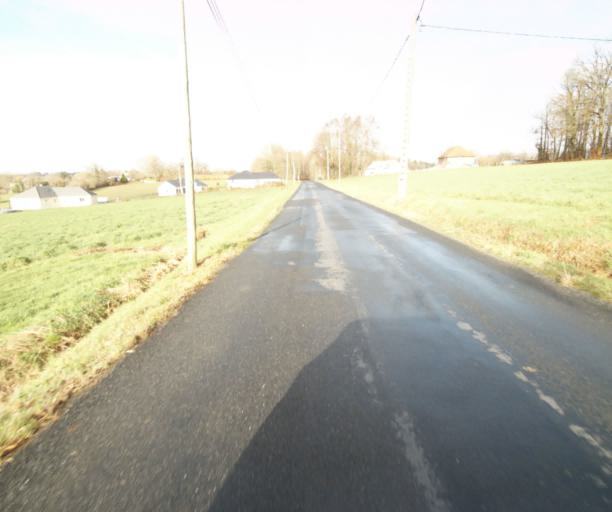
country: FR
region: Limousin
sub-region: Departement de la Correze
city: Saint-Mexant
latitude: 45.2799
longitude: 1.6033
